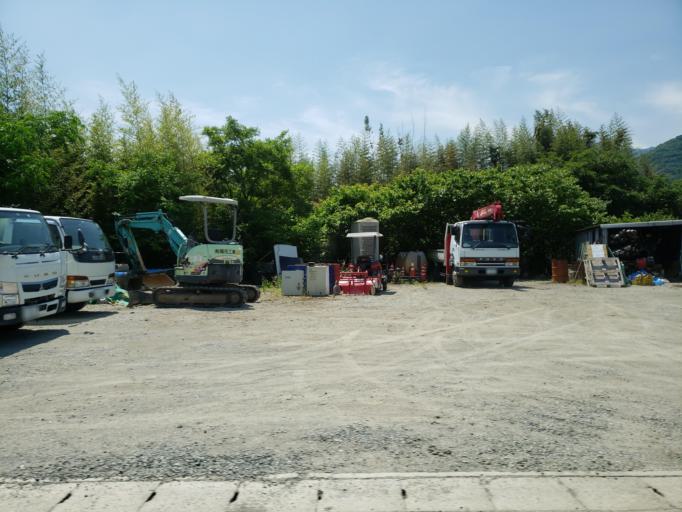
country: JP
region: Tokushima
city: Wakimachi
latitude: 34.0706
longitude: 134.1972
